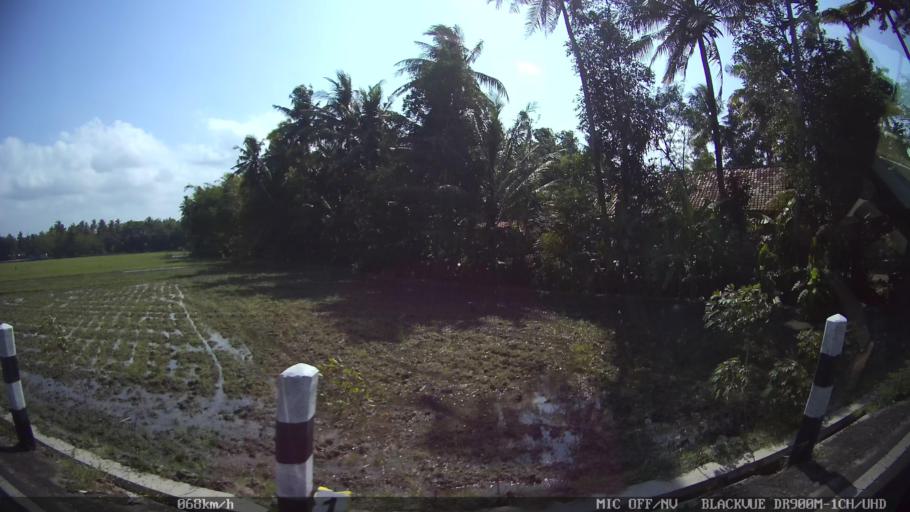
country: ID
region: Daerah Istimewa Yogyakarta
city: Srandakan
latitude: -7.9285
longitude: 110.1917
